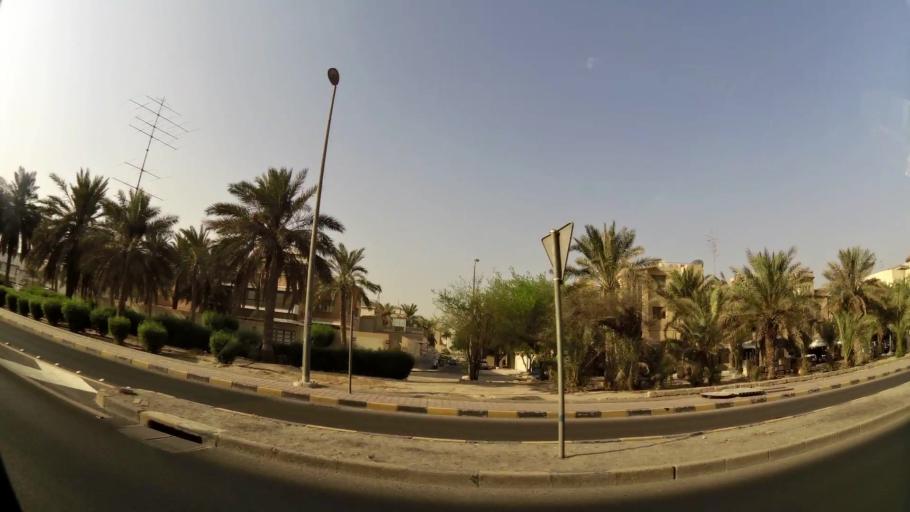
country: KW
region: Muhafazat Hawalli
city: Hawalli
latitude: 29.3532
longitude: 48.0252
